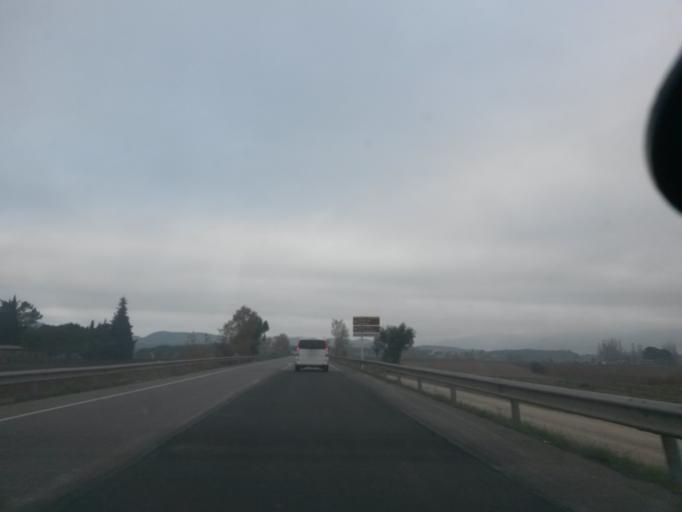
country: ES
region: Catalonia
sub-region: Provincia de Girona
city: Banyoles
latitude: 42.1380
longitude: 2.7688
